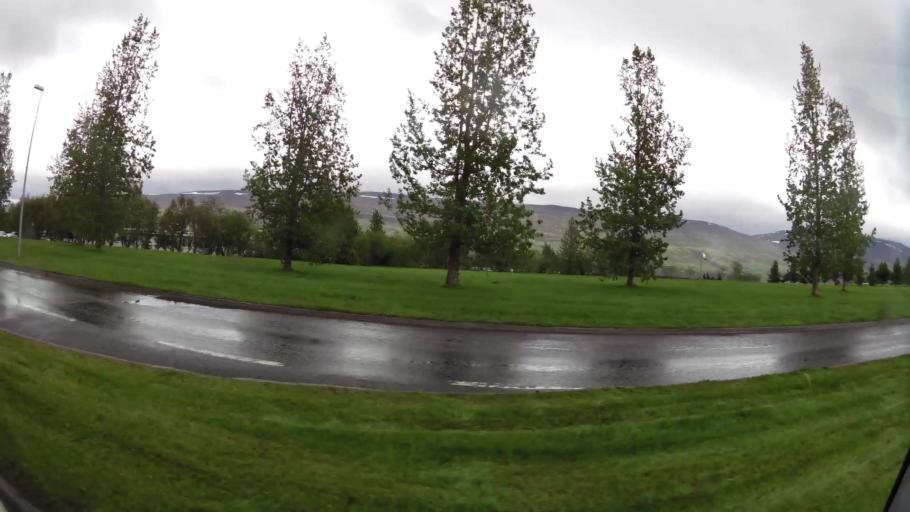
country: IS
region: Northeast
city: Akureyri
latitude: 65.6725
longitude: -18.0964
